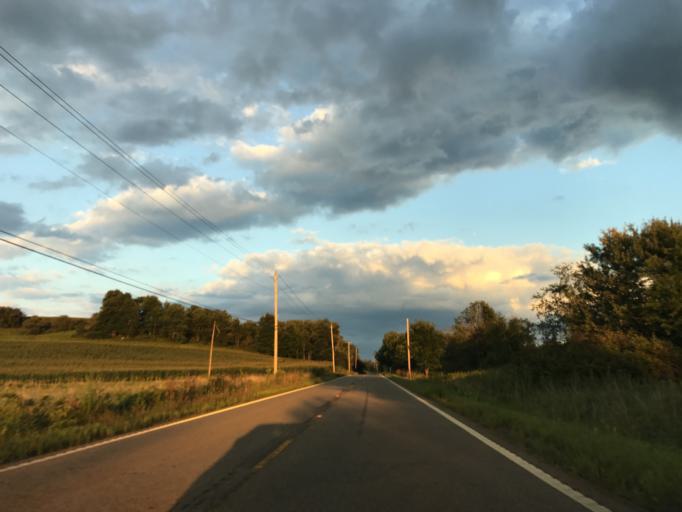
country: US
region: Ohio
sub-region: Stark County
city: Minerva
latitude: 40.7449
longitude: -81.0267
